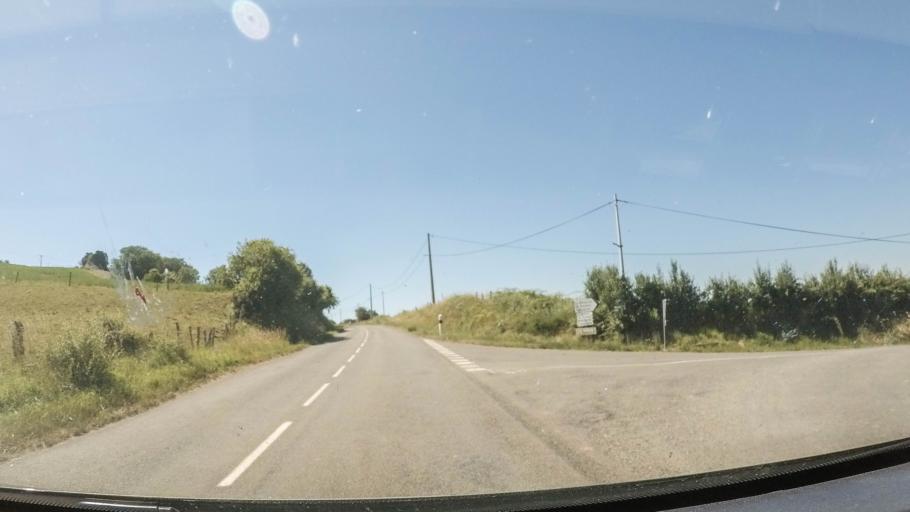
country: FR
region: Midi-Pyrenees
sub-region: Departement de l'Aveyron
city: Saint-Christophe-Vallon
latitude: 44.4700
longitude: 2.3675
